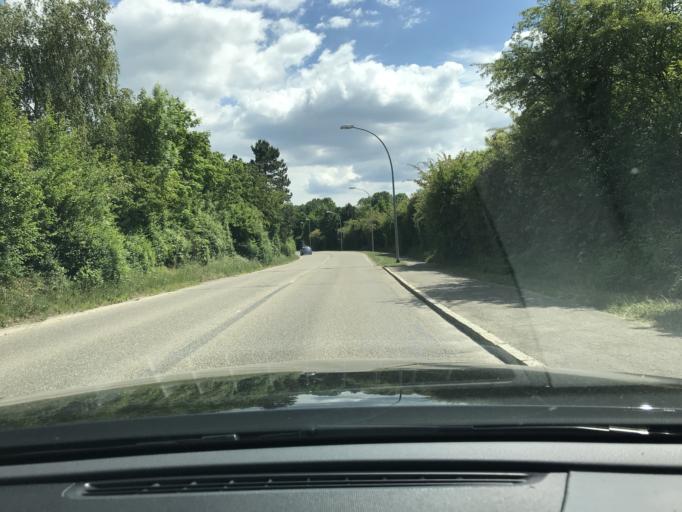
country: DE
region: Baden-Wuerttemberg
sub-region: Regierungsbezirk Stuttgart
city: Schwaikheim
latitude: 48.8726
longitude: 9.3590
